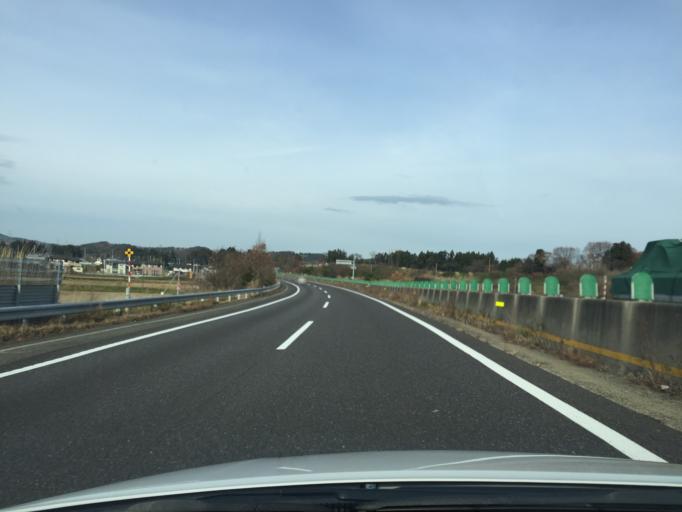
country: JP
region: Fukushima
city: Nihommatsu
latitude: 37.6114
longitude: 140.4229
